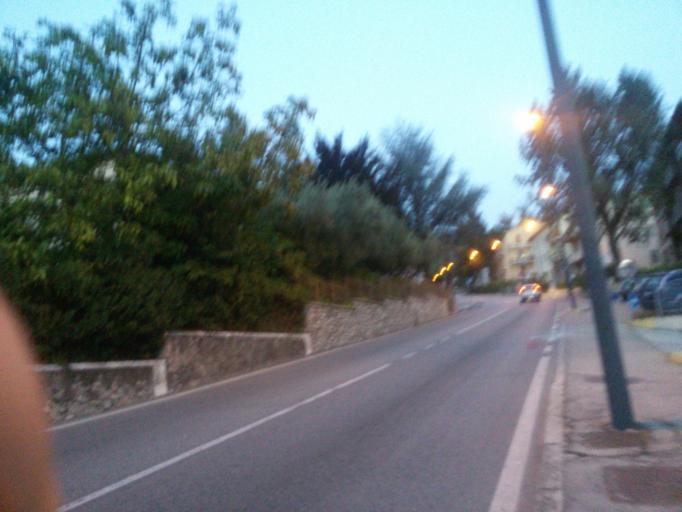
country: IT
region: Umbria
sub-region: Provincia di Perugia
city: Spoleto
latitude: 42.7321
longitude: 12.7314
